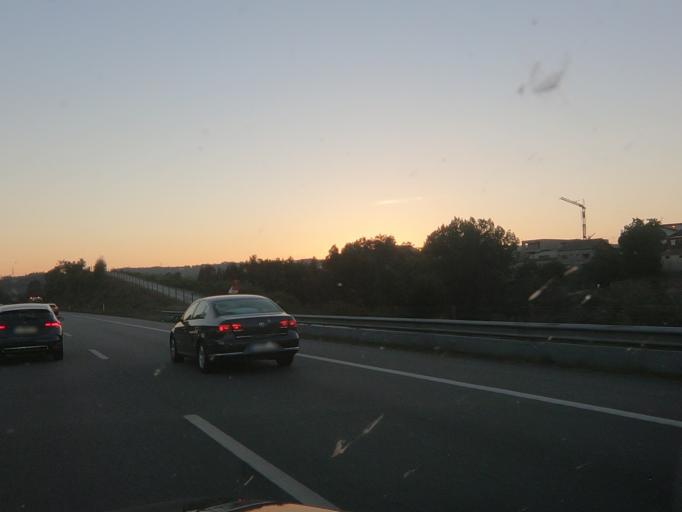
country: PT
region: Porto
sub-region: Paredes
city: Paredes
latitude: 41.2000
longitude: -8.3229
